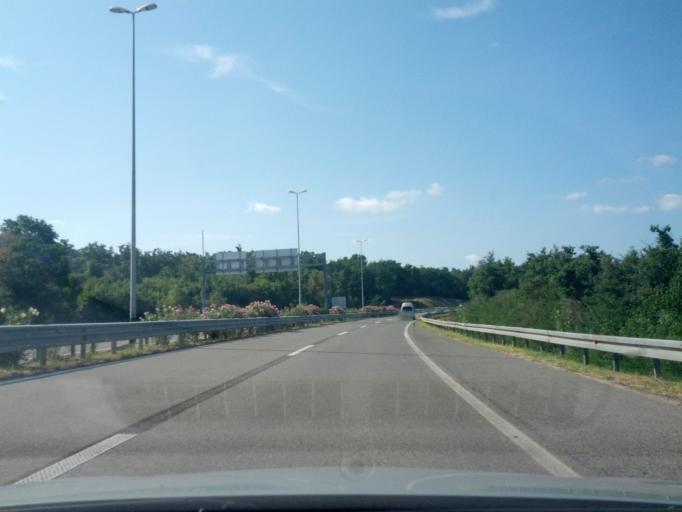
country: HR
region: Istarska
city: Buje
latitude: 45.3988
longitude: 13.6235
